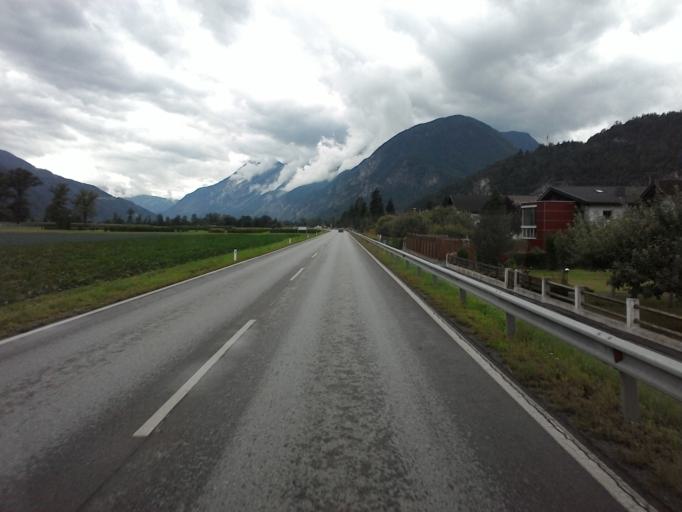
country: AT
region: Tyrol
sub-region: Politischer Bezirk Imst
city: Stams
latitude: 47.2804
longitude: 10.9801
